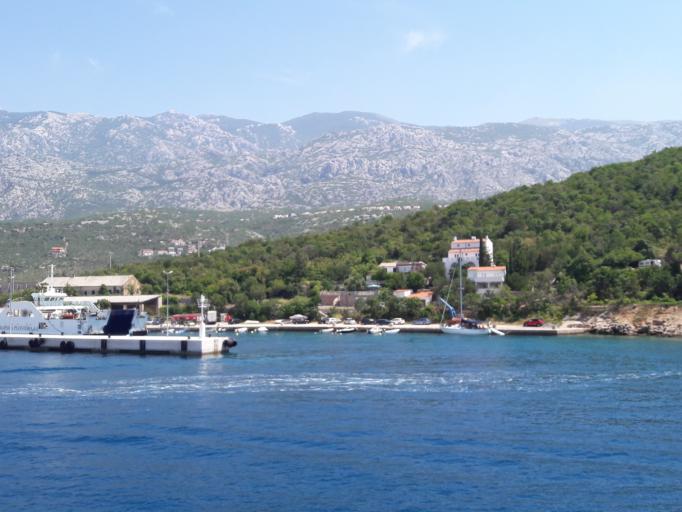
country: HR
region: Primorsko-Goranska
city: Banjol
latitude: 44.7189
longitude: 14.8897
